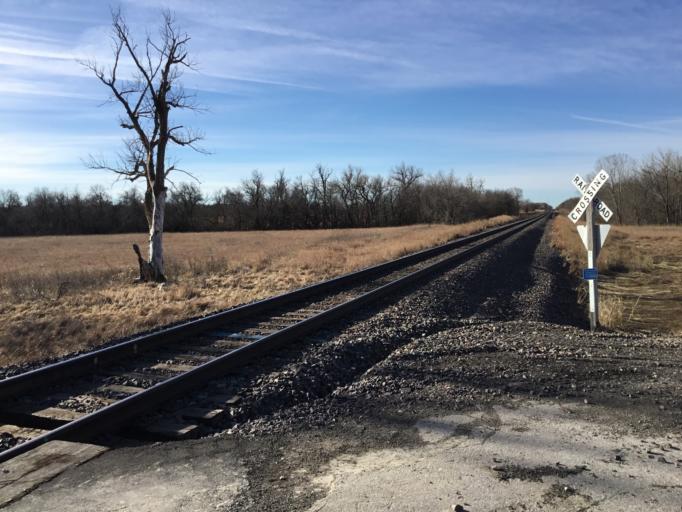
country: US
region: Kansas
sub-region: Marion County
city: Hillsboro
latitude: 38.4060
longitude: -97.4056
